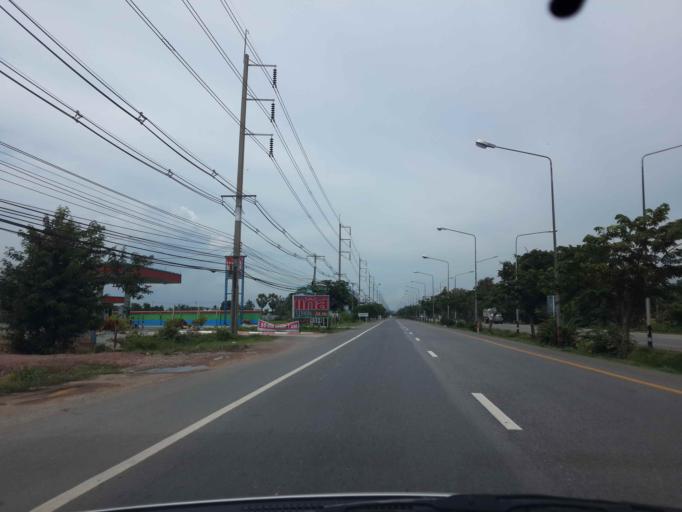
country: TH
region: Ratchaburi
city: Pak Tho
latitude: 13.3534
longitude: 99.8271
